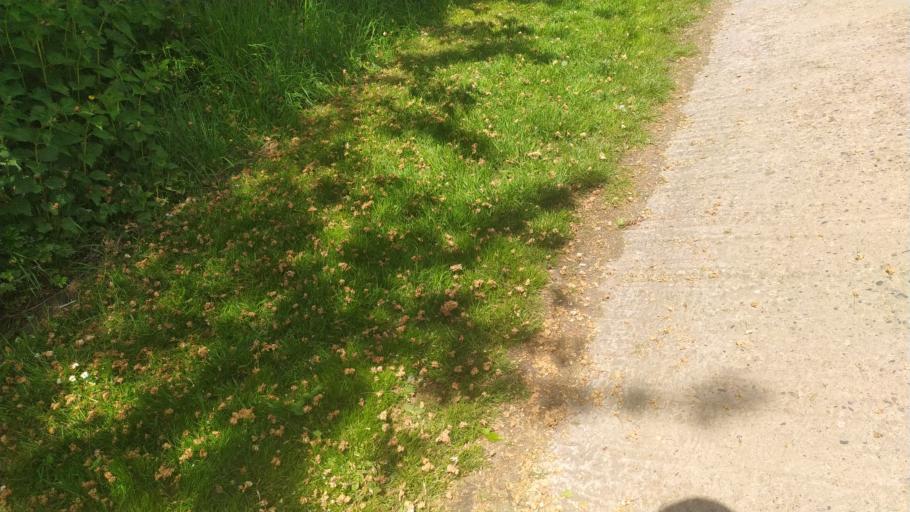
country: GB
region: England
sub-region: North Yorkshire
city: Pannal
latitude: 53.8967
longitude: -1.5356
